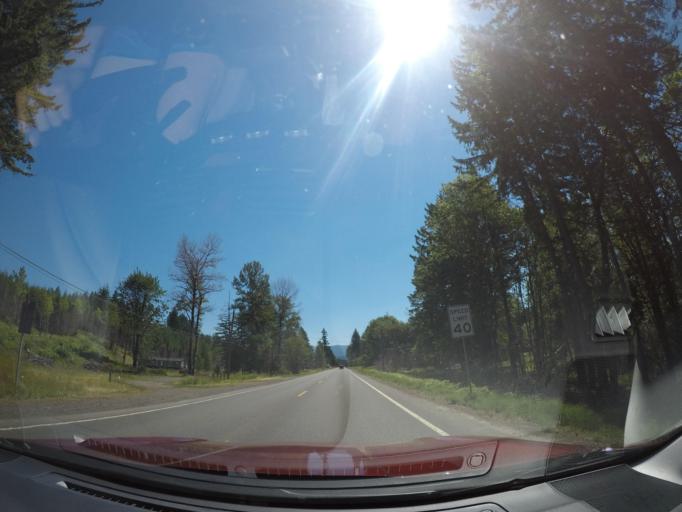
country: US
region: Oregon
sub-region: Linn County
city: Mill City
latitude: 44.7569
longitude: -122.4308
